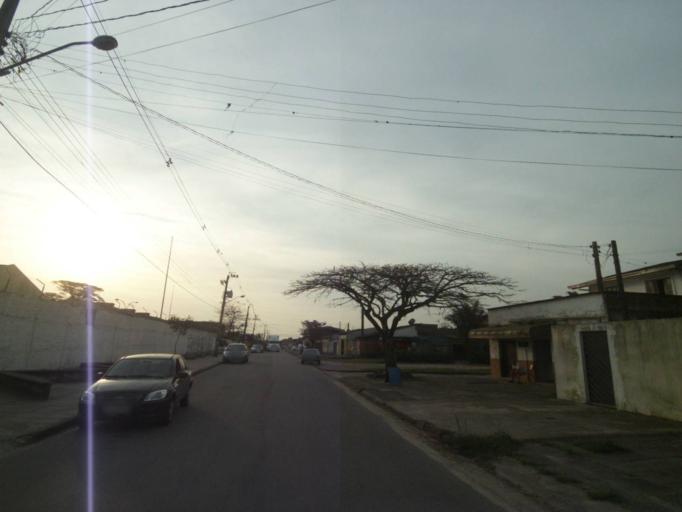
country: BR
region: Parana
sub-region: Paranagua
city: Paranagua
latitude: -25.5263
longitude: -48.5320
